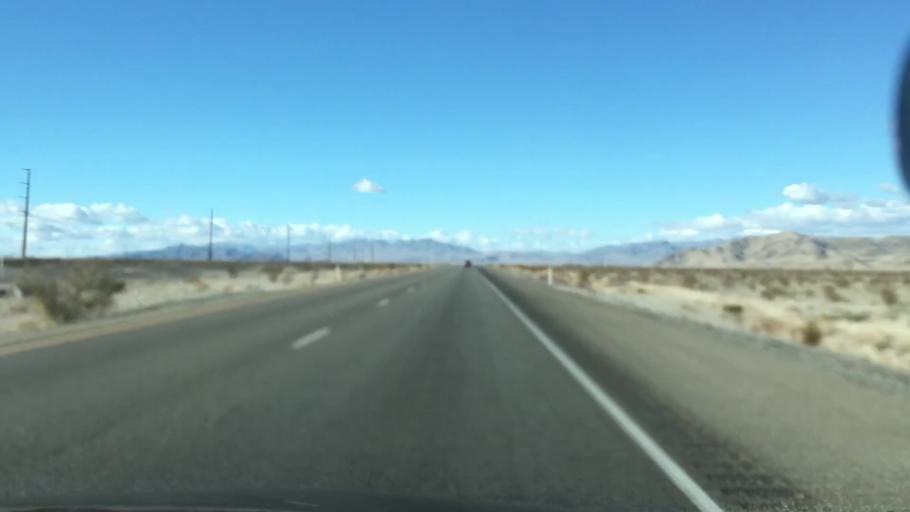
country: US
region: Nevada
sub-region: Clark County
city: Summerlin South
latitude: 36.5509
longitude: -115.5947
